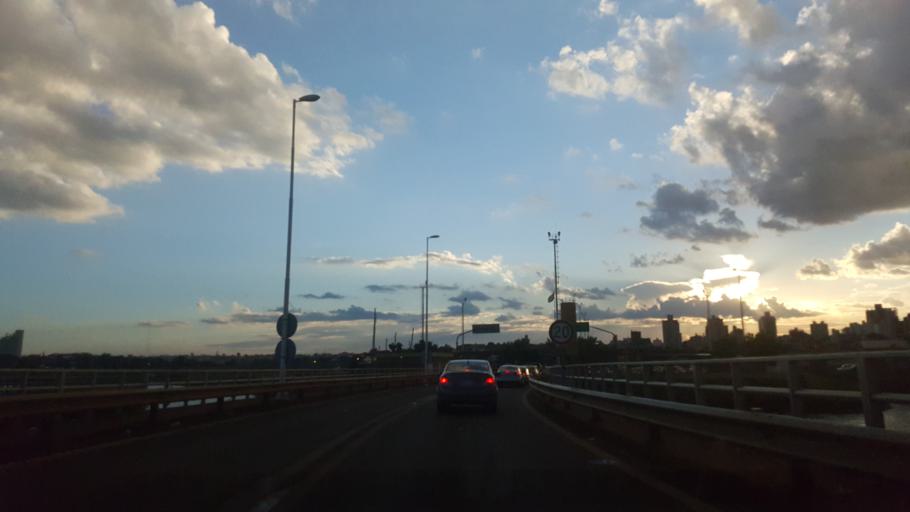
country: AR
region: Misiones
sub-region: Departamento de Capital
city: Posadas
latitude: -27.3762
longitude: -55.8798
